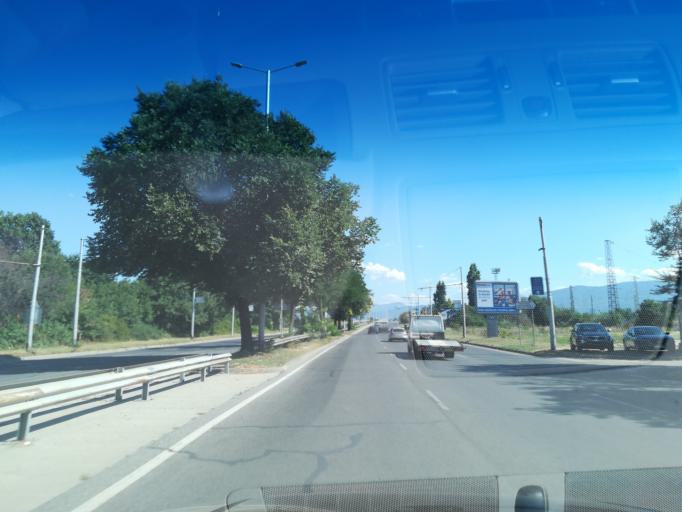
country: BG
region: Plovdiv
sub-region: Obshtina Plovdiv
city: Plovdiv
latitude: 42.1218
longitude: 24.7739
